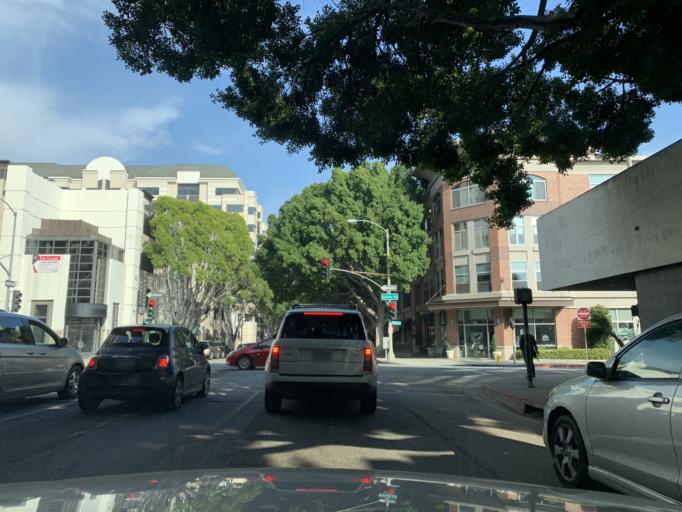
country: US
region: California
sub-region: Los Angeles County
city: Pasadena
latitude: 34.1445
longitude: -118.1343
